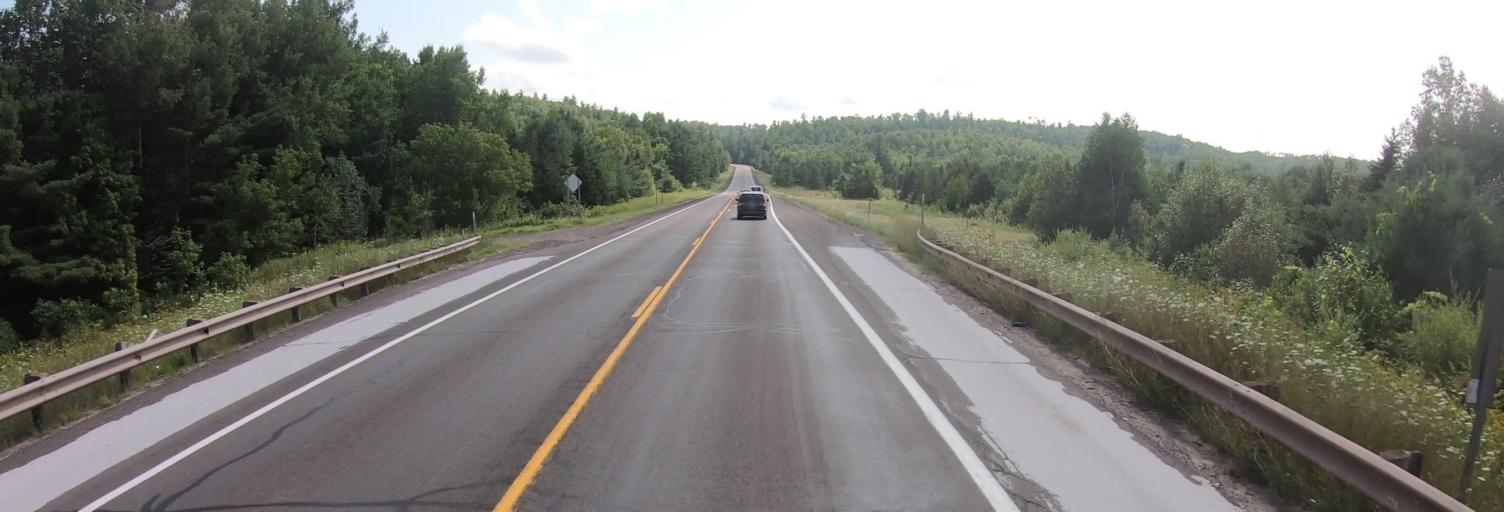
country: US
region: Michigan
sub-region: Ontonagon County
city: Ontonagon
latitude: 46.6985
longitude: -89.1608
